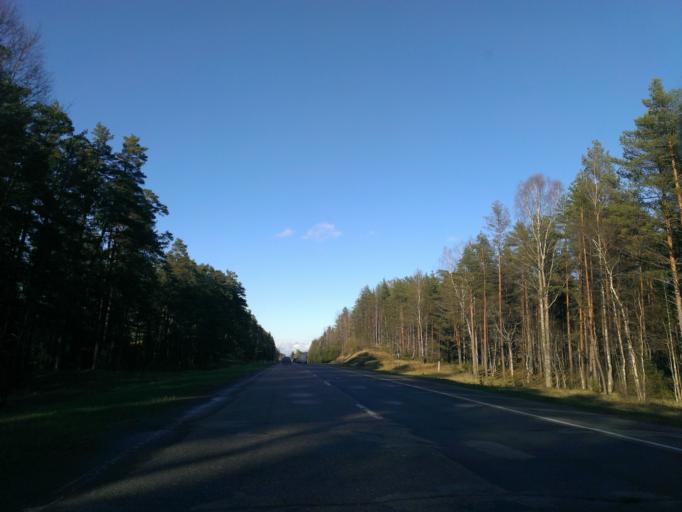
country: LV
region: Incukalns
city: Vangazi
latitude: 57.0824
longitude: 24.5314
